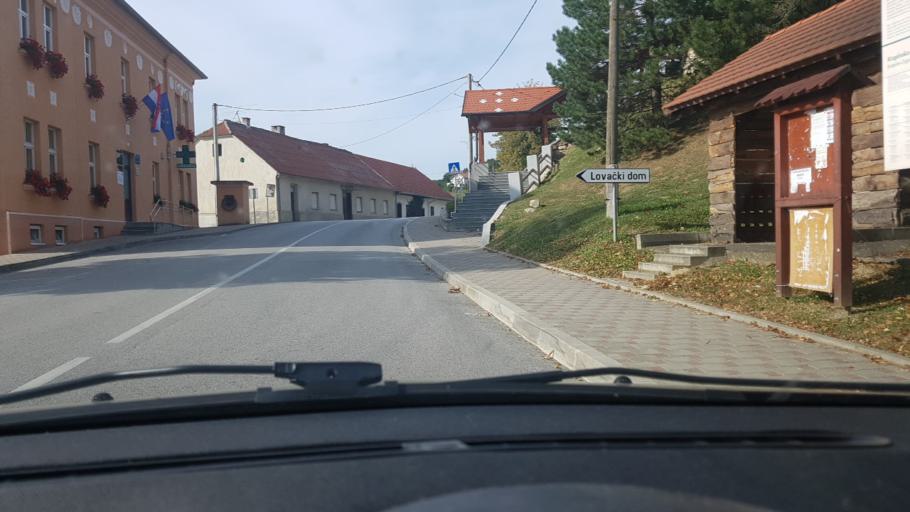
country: HR
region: Krapinsko-Zagorska
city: Mihovljan
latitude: 46.1330
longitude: 15.9701
